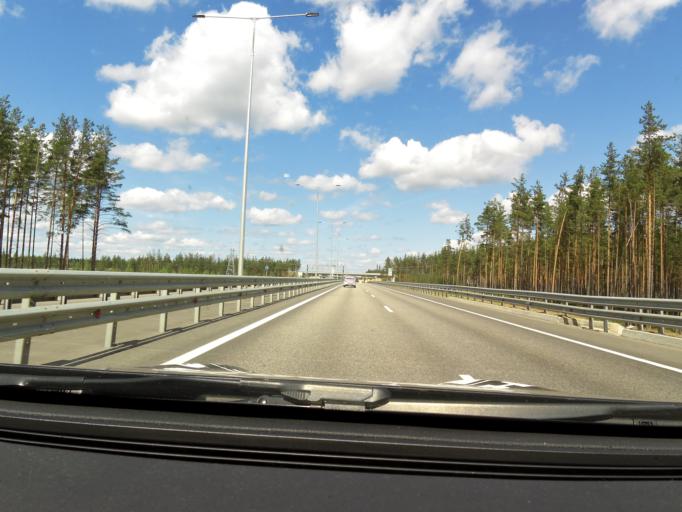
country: RU
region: Tverskaya
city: Bologoye
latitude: 57.6955
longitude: 34.2091
